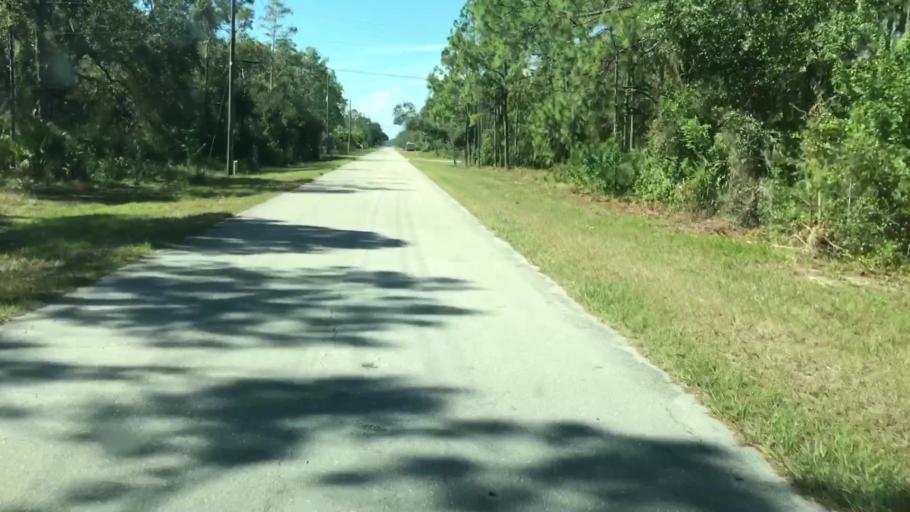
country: US
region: Florida
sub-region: Lee County
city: Lehigh Acres
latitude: 26.6619
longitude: -81.6159
